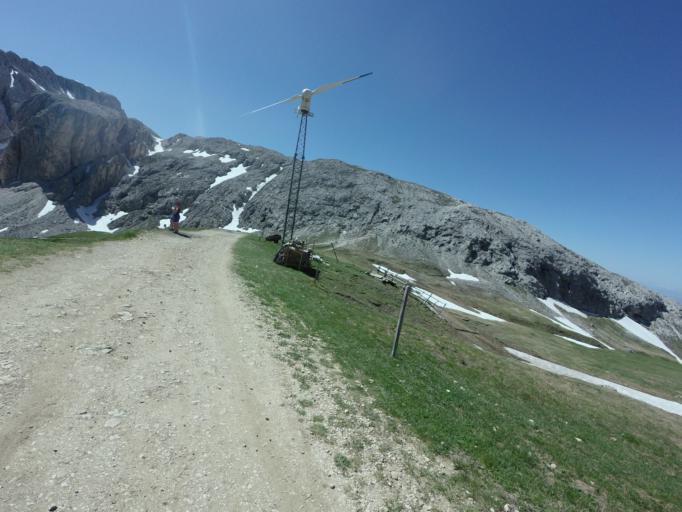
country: IT
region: Trentino-Alto Adige
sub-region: Provincia di Trento
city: Mazzin
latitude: 46.4971
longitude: 11.6338
